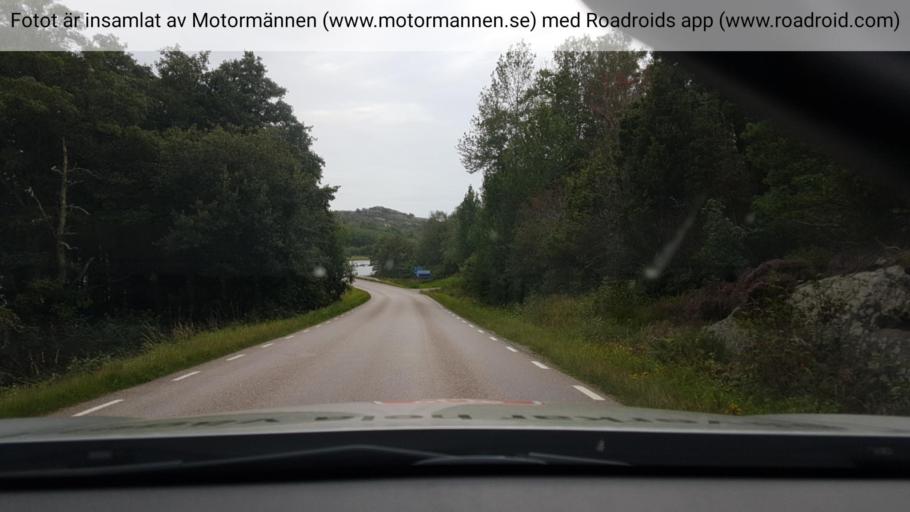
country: SE
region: Vaestra Goetaland
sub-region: Tanums Kommun
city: Grebbestad
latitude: 58.6200
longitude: 11.2874
